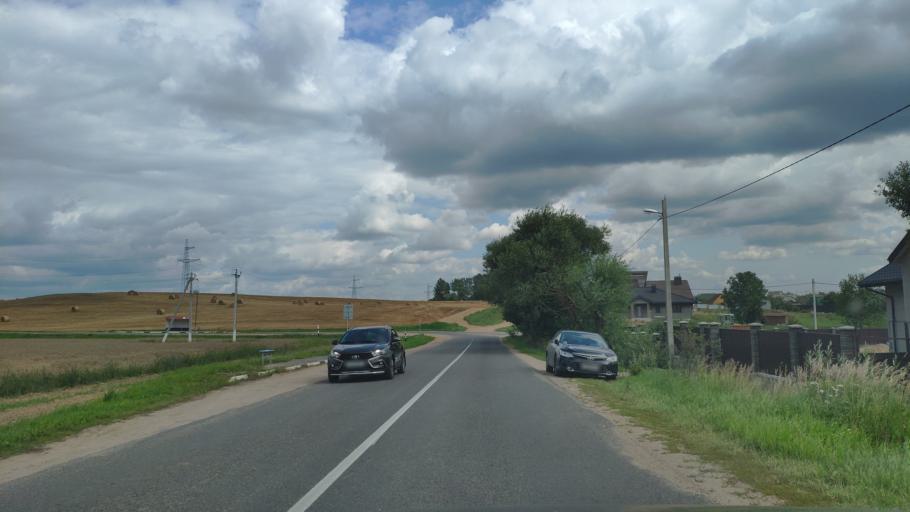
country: BY
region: Minsk
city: Khatsyezhyna
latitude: 53.8694
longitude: 27.3168
